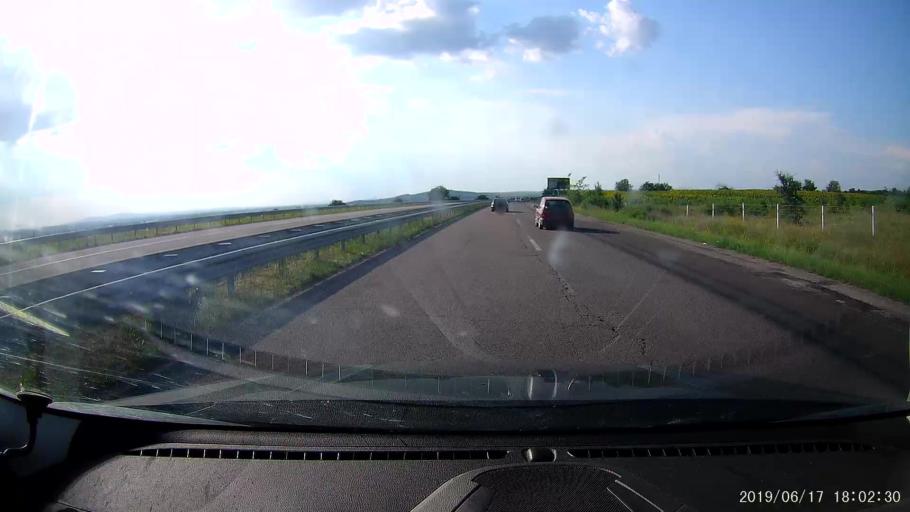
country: BG
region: Khaskovo
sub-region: Obshtina Svilengrad
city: Svilengrad
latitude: 41.7607
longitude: 26.2299
